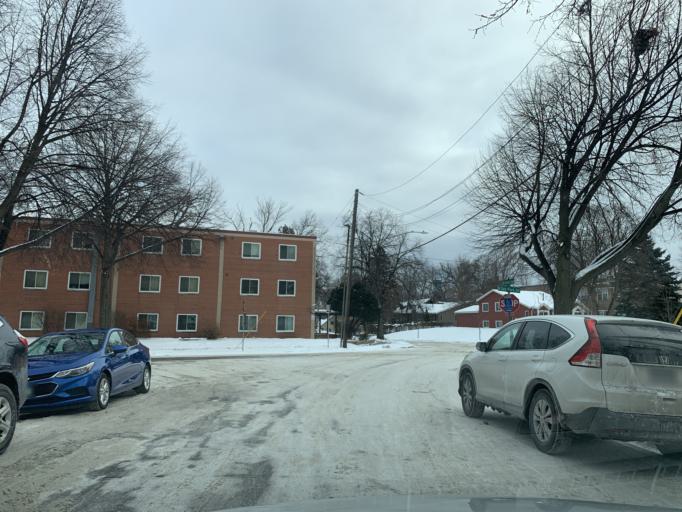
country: US
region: Minnesota
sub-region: Hennepin County
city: Minneapolis
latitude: 44.9878
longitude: -93.3024
